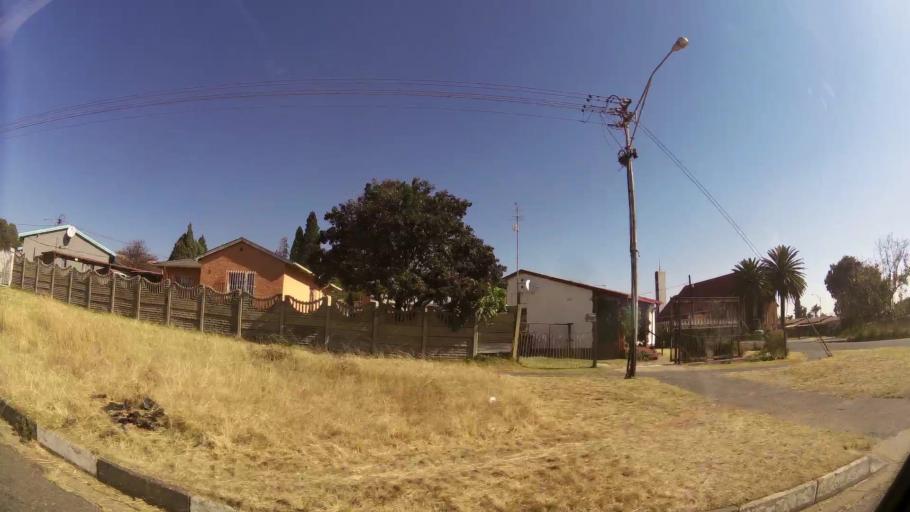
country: ZA
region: Gauteng
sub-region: City of Johannesburg Metropolitan Municipality
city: Johannesburg
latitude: -26.2526
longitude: 28.0880
